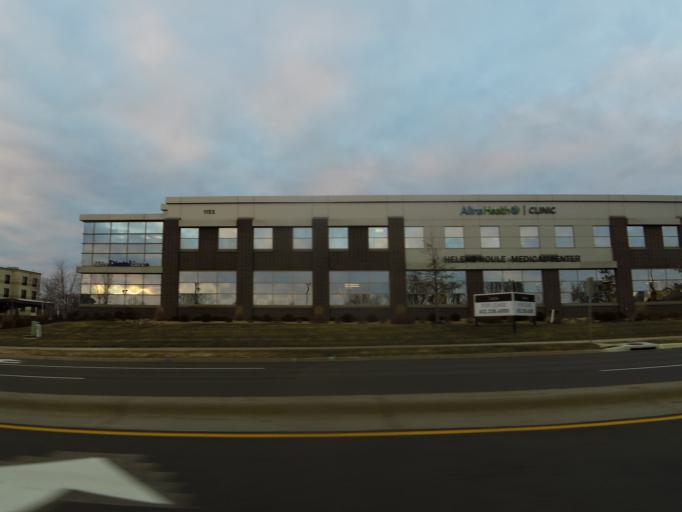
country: US
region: Minnesota
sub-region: Ramsey County
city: Vadnais Heights
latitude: 45.0503
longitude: -93.0524
